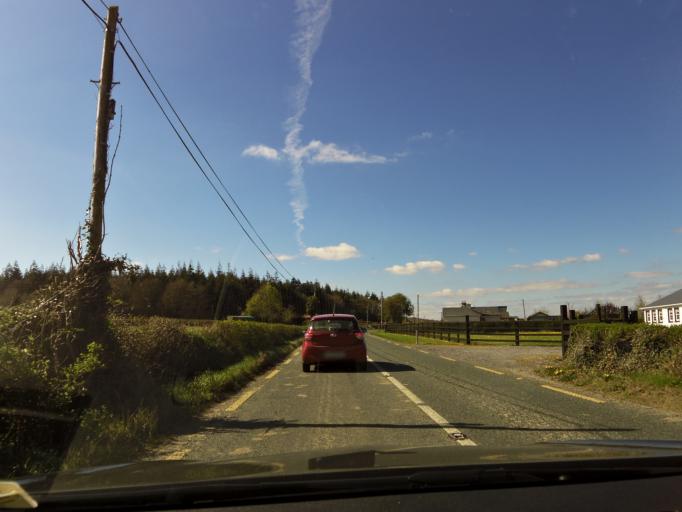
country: IE
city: Ballylinan
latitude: 53.0043
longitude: -7.0744
